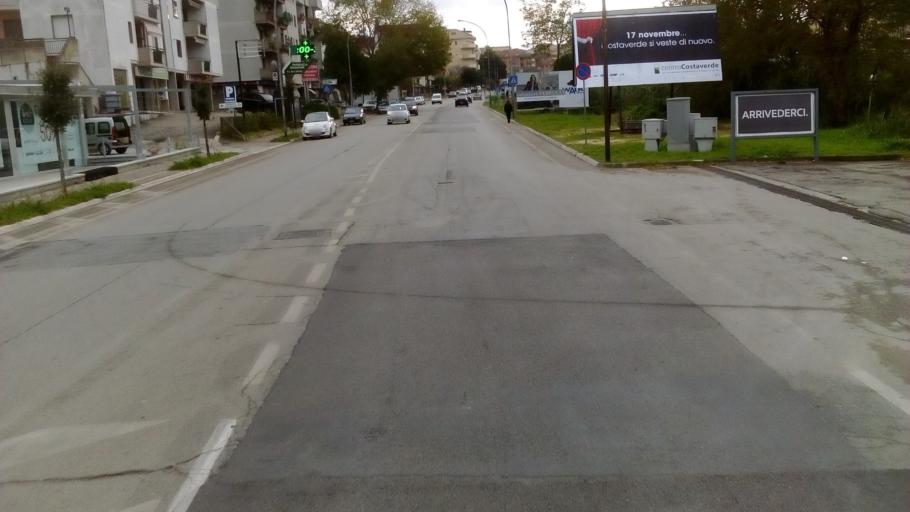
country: IT
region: Abruzzo
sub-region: Provincia di Chieti
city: Vasto
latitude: 42.1105
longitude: 14.7013
